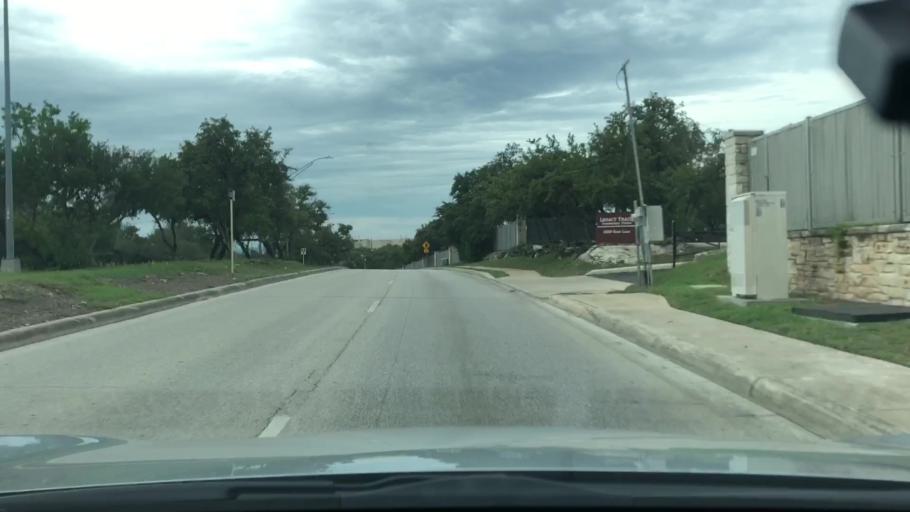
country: US
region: Texas
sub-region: Bexar County
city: Leon Valley
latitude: 29.4641
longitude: -98.6739
